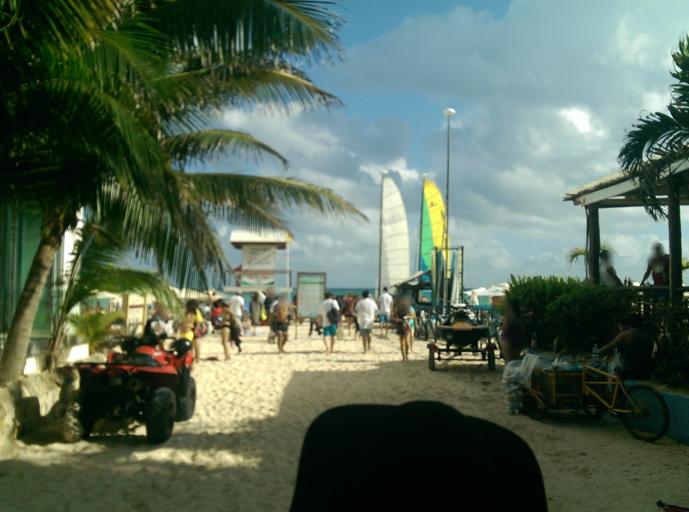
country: MX
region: Quintana Roo
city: Playa del Carmen
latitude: 20.6310
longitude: -87.0654
